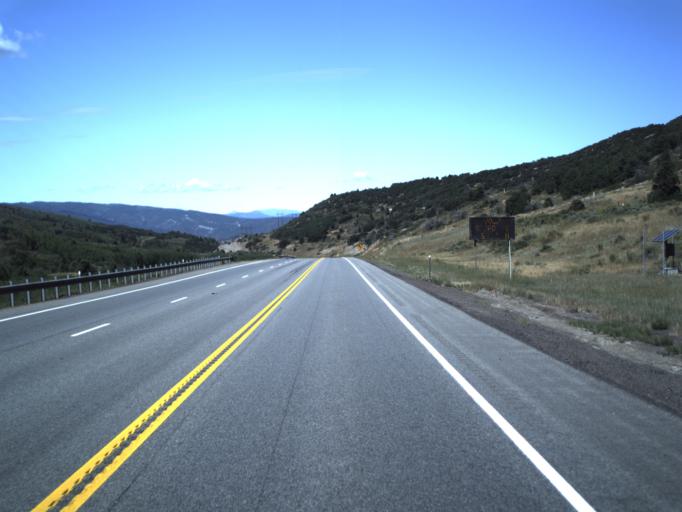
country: US
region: Utah
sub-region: Carbon County
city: Helper
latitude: 39.9338
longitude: -111.0980
